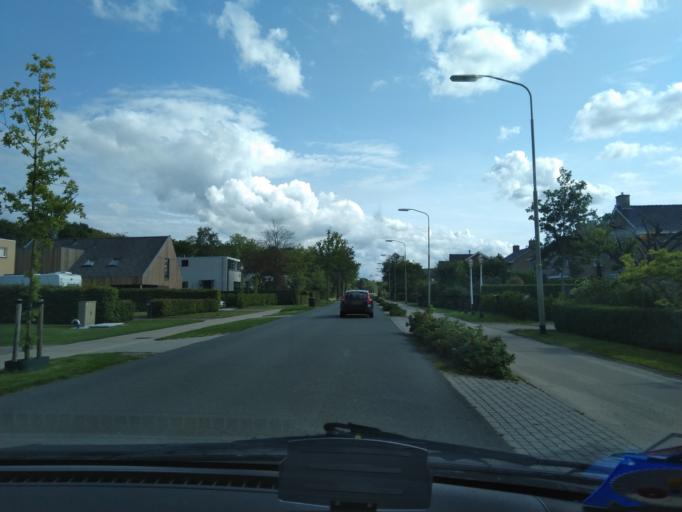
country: NL
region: Groningen
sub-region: Gemeente Groningen
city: Groningen
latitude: 53.1754
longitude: 6.5450
